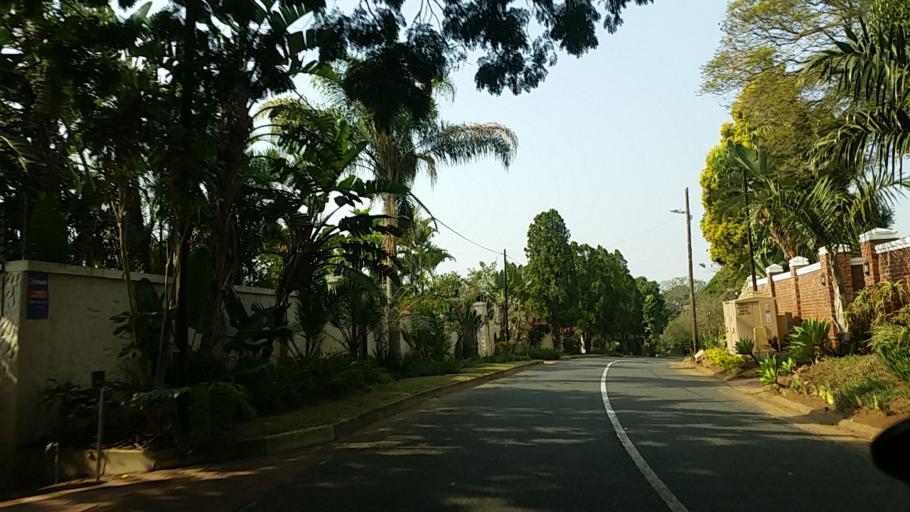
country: ZA
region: KwaZulu-Natal
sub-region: eThekwini Metropolitan Municipality
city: Berea
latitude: -29.8331
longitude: 30.9284
